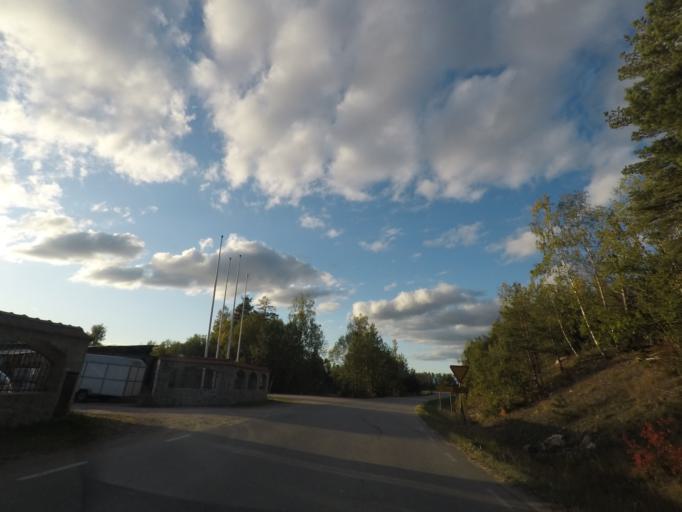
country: SE
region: Vaestmanland
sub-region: Kopings Kommun
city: Koping
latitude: 59.5102
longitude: 16.0637
